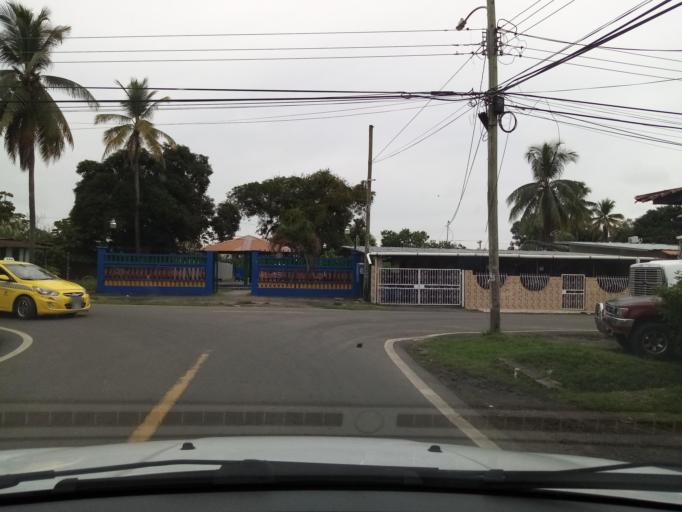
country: PA
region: Panama
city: Pacora
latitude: 9.0818
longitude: -79.2886
